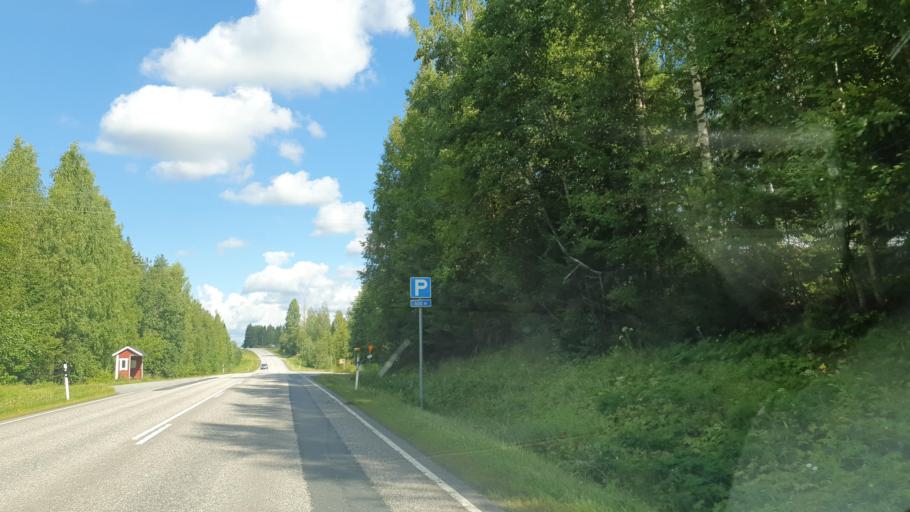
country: FI
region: Northern Savo
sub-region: Ylae-Savo
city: Sonkajaervi
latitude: 63.7394
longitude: 27.3805
